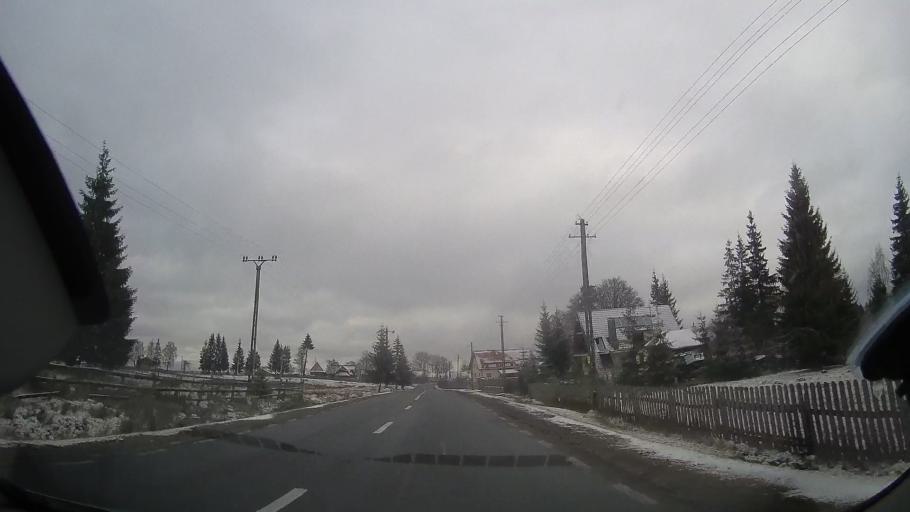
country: RO
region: Cluj
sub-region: Comuna Belis
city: Belis
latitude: 46.7054
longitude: 23.0379
